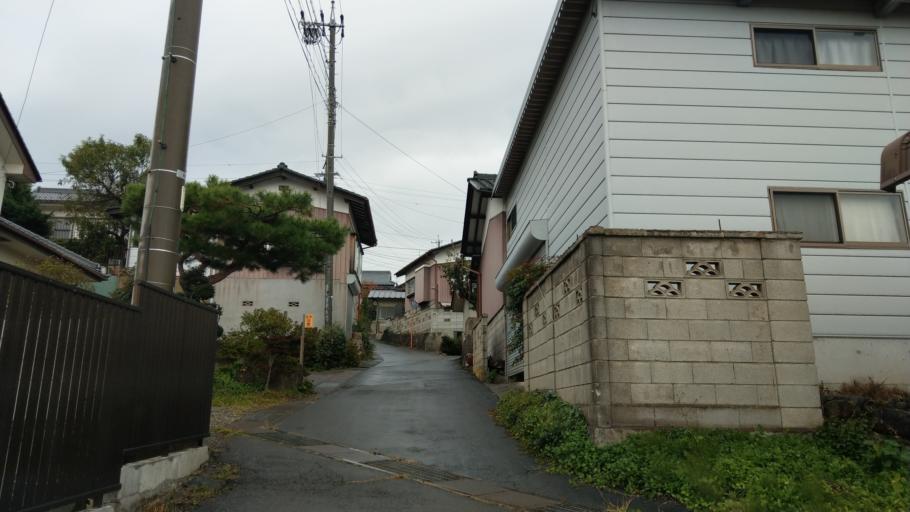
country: JP
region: Nagano
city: Komoro
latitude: 36.3475
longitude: 138.4101
